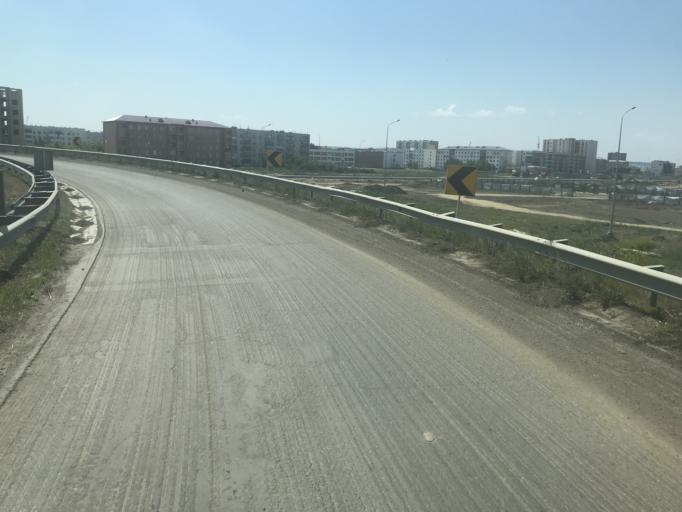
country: KZ
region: Aqmola
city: Kokshetau
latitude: 53.3184
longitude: 69.3949
